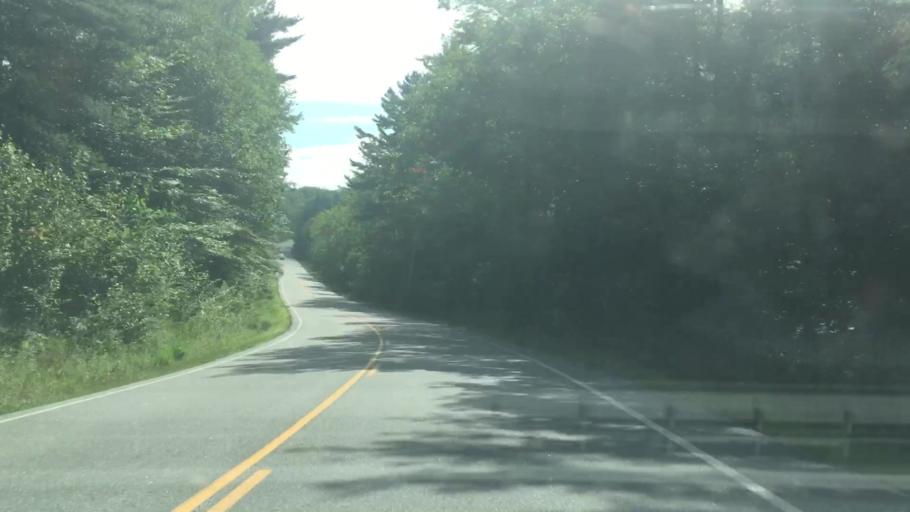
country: US
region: Maine
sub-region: Androscoggin County
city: Poland
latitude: 44.0212
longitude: -70.4404
